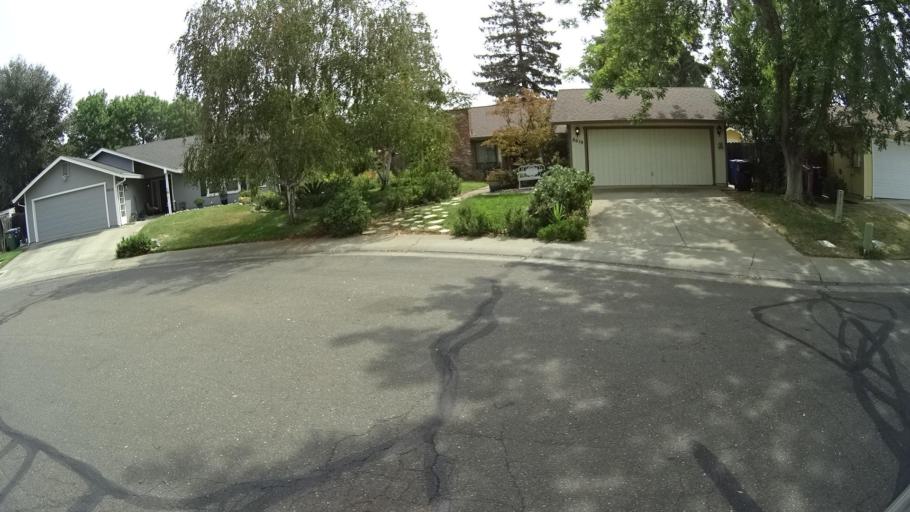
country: US
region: California
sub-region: Sacramento County
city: Elk Grove
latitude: 38.4144
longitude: -121.3860
